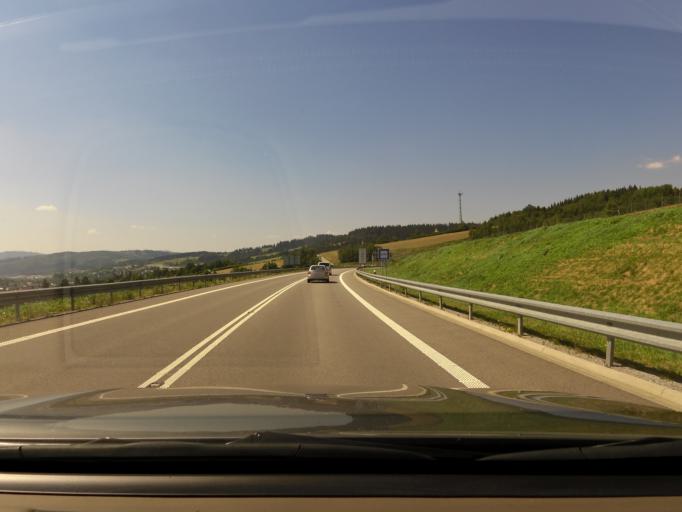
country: SK
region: Zilinsky
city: Cadca
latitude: 49.4908
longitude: 18.8012
